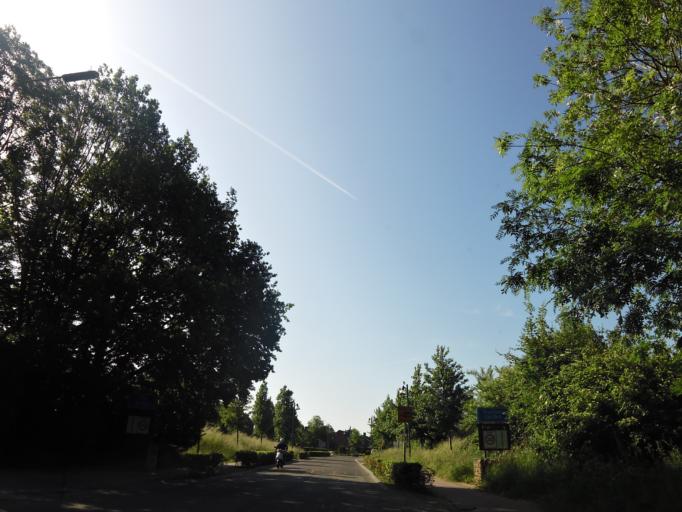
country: NL
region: Limburg
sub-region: Gemeente Voerendaal
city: Ubachsberg
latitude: 50.8571
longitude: 5.9431
